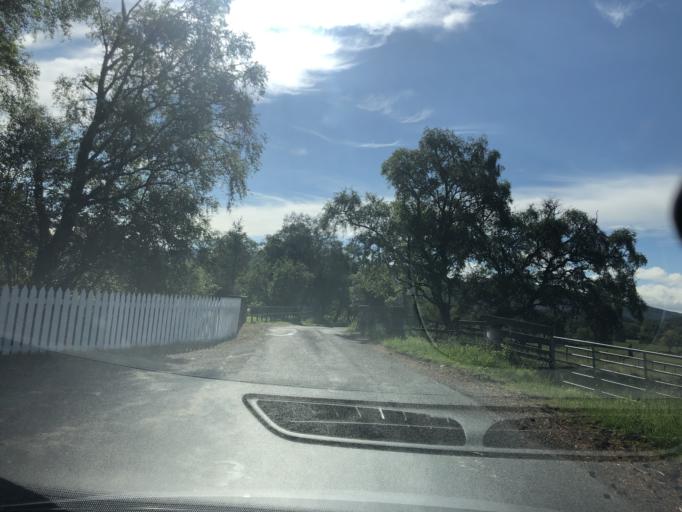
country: GB
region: Scotland
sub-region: Angus
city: Kirriemuir
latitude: 56.8356
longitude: -3.0814
